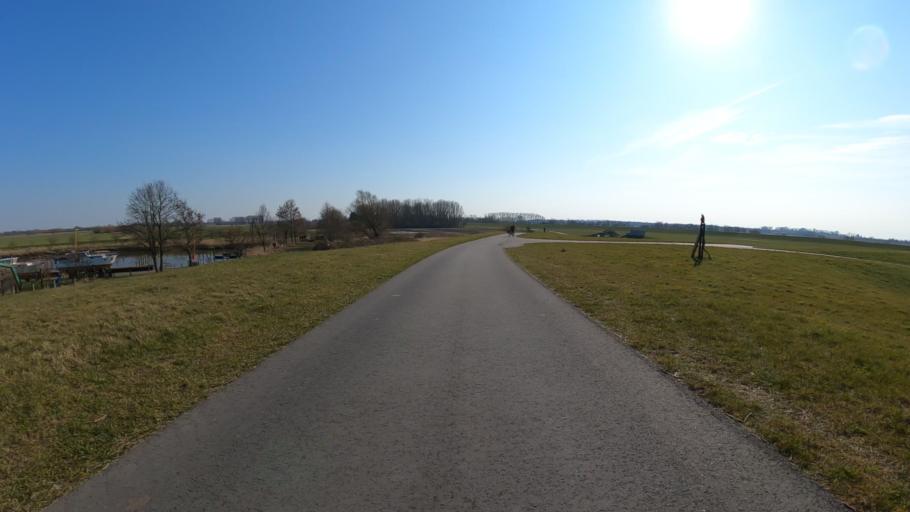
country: DE
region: Schleswig-Holstein
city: Seestermuhe
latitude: 53.7158
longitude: 9.5265
